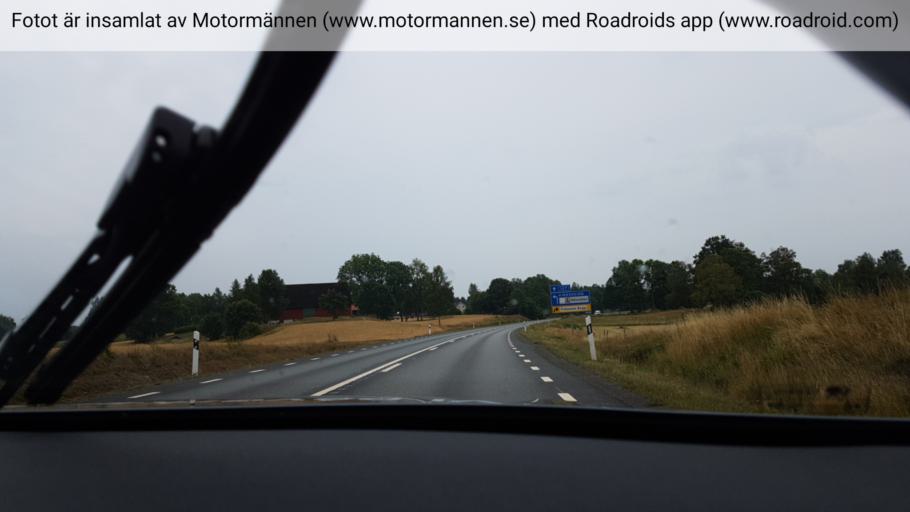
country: SE
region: Joenkoeping
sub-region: Varnamo Kommun
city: Varnamo
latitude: 57.2065
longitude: 14.1013
